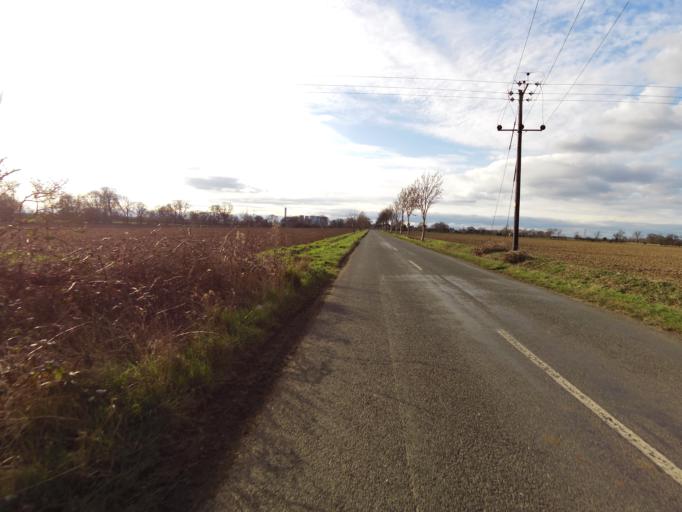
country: GB
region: England
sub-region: East Riding of Yorkshire
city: Snaith
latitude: 53.7109
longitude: -1.0636
